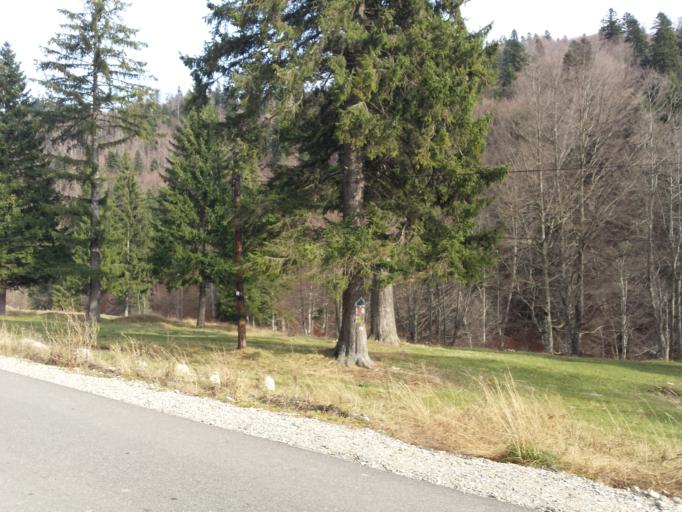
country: RO
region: Prahova
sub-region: Oras Azuga
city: Azuga
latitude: 45.4362
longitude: 25.5294
